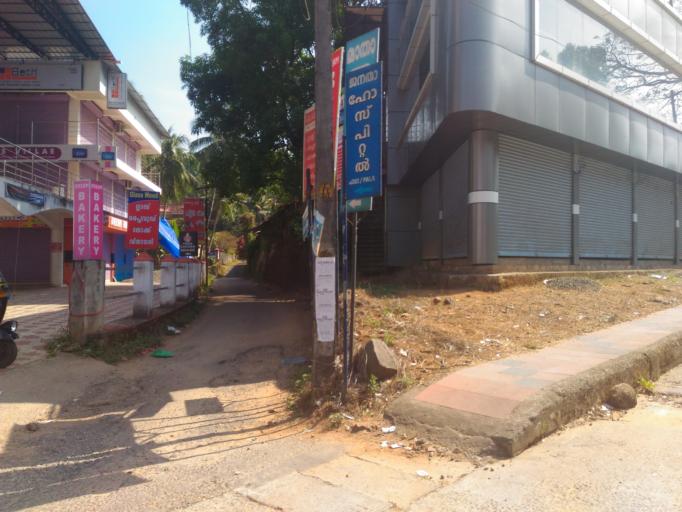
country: IN
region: Kerala
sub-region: Kottayam
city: Lalam
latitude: 9.7127
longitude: 76.6901
